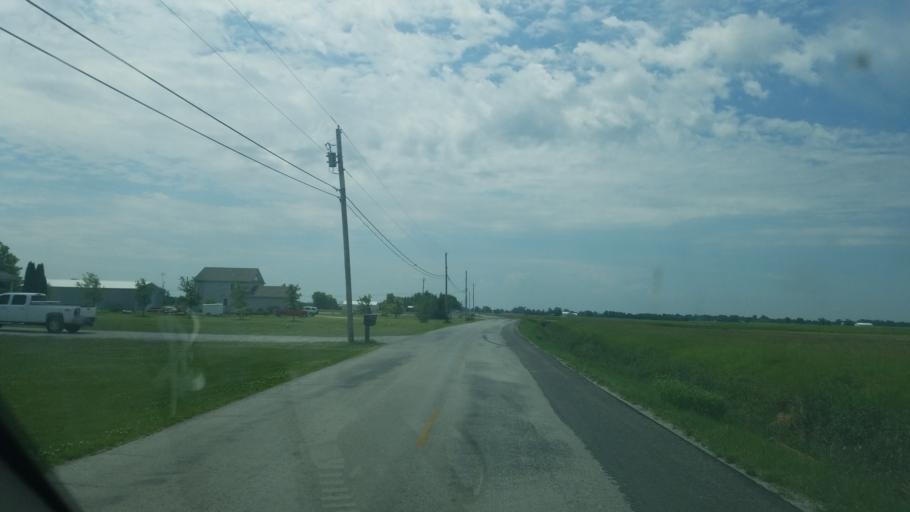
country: US
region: Ohio
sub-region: Wood County
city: Bowling Green
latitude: 41.2840
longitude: -83.5928
